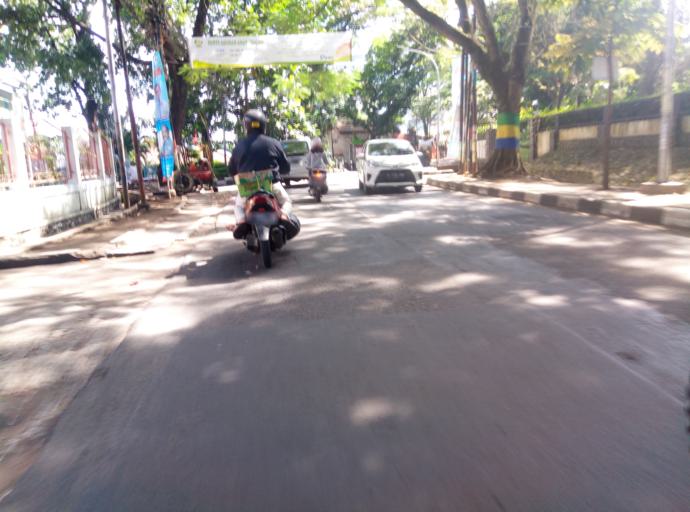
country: ID
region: West Java
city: Bandung
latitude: -6.8851
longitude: 107.6162
